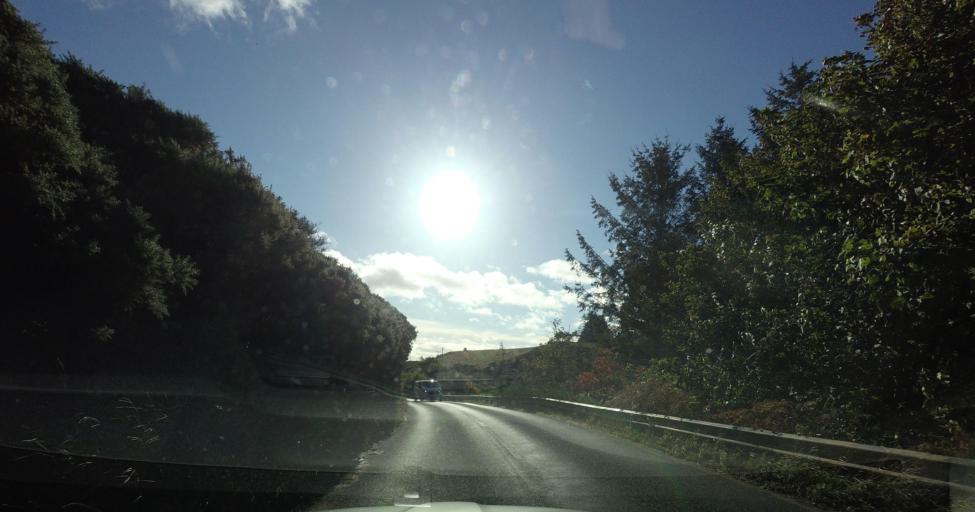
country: GB
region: Scotland
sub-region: Aberdeenshire
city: Macduff
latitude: 57.6607
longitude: -2.3557
